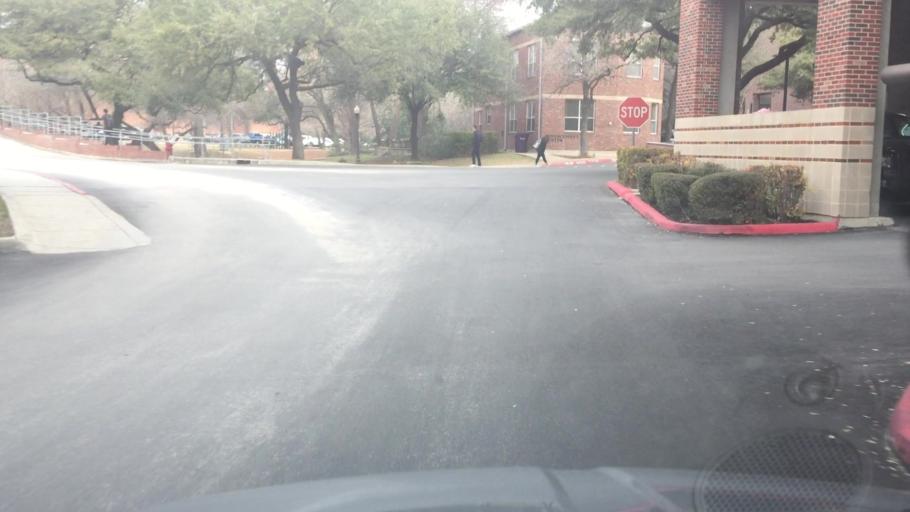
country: US
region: Texas
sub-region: Bexar County
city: Alamo Heights
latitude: 29.4665
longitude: -98.4678
